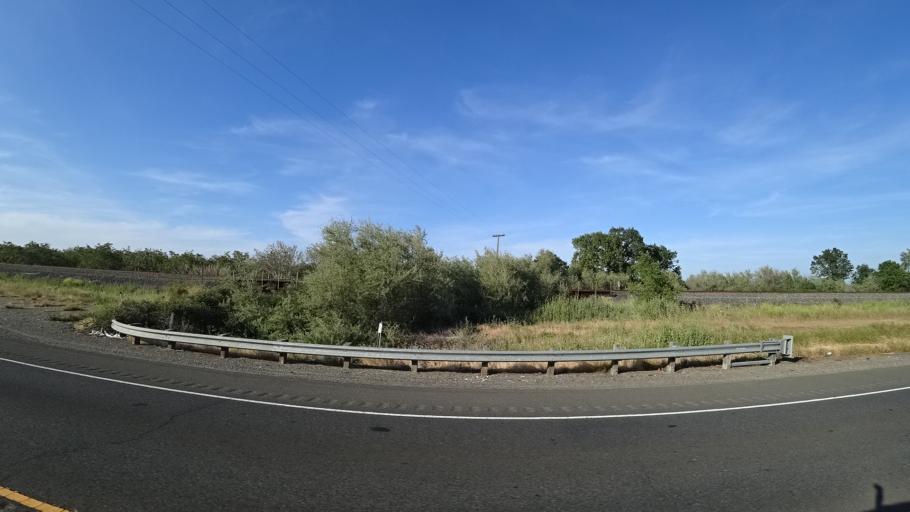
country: US
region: California
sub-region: Placer County
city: Sheridan
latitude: 38.9943
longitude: -121.3969
